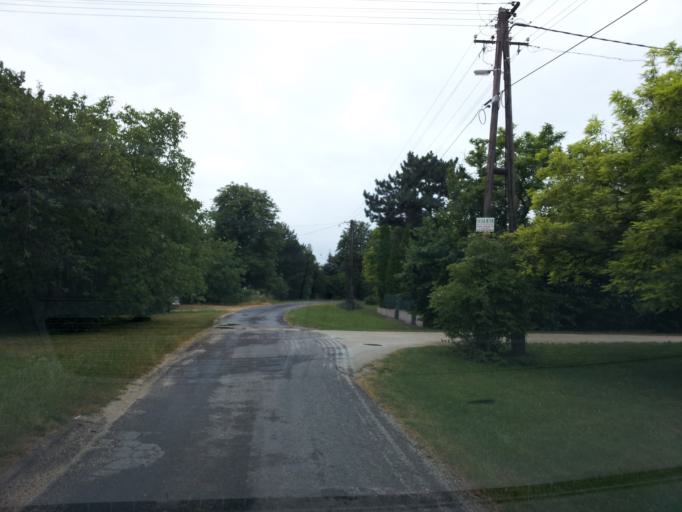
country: HU
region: Veszprem
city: Balatonkenese
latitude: 47.0152
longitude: 18.1602
